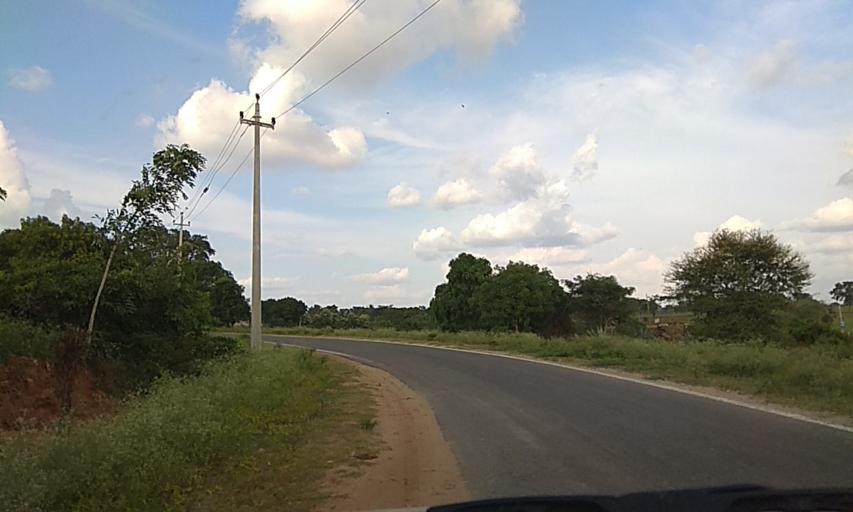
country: IN
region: Karnataka
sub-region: Chamrajnagar
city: Gundlupet
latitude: 11.7620
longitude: 76.7763
